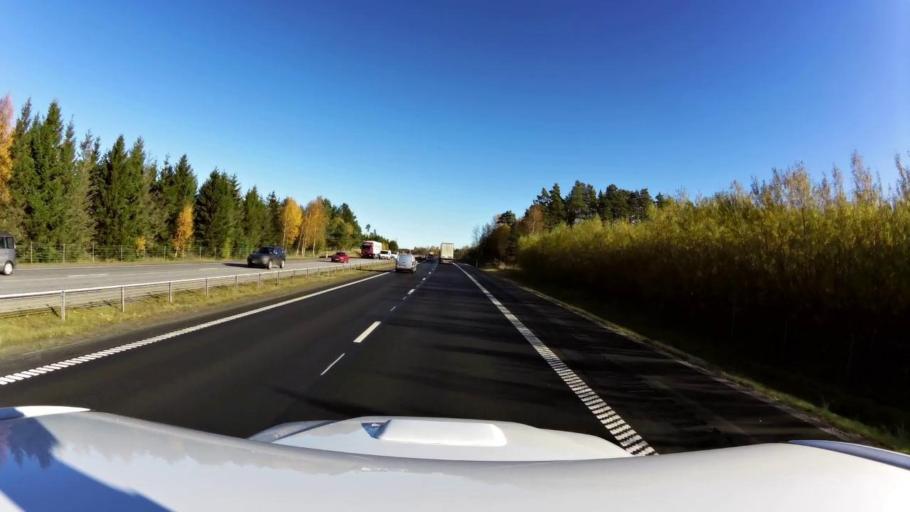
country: SE
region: OEstergoetland
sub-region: Linkopings Kommun
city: Vikingstad
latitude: 58.3921
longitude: 15.4159
